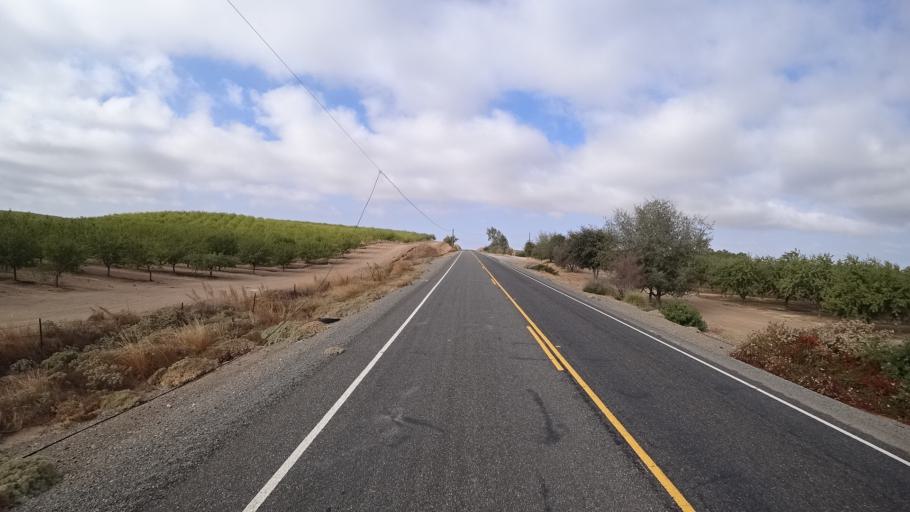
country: US
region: California
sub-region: Yolo County
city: Dunnigan
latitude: 38.7944
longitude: -121.9025
